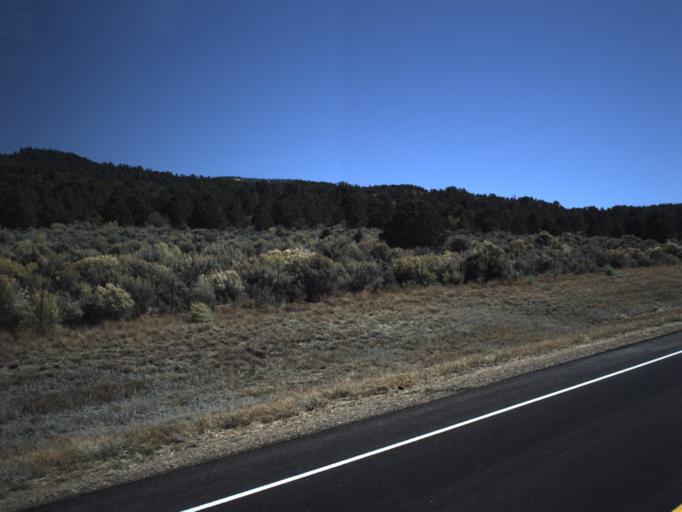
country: US
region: Utah
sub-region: Garfield County
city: Panguitch
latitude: 37.6452
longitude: -111.8452
